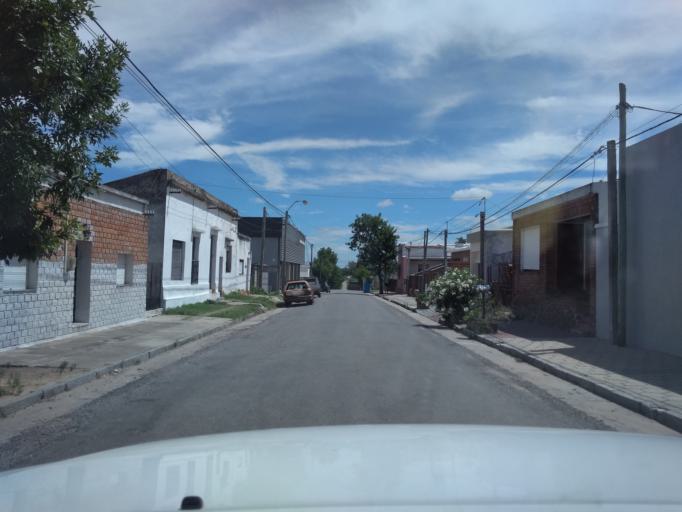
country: UY
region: Florida
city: Florida
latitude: -34.1036
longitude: -56.2170
